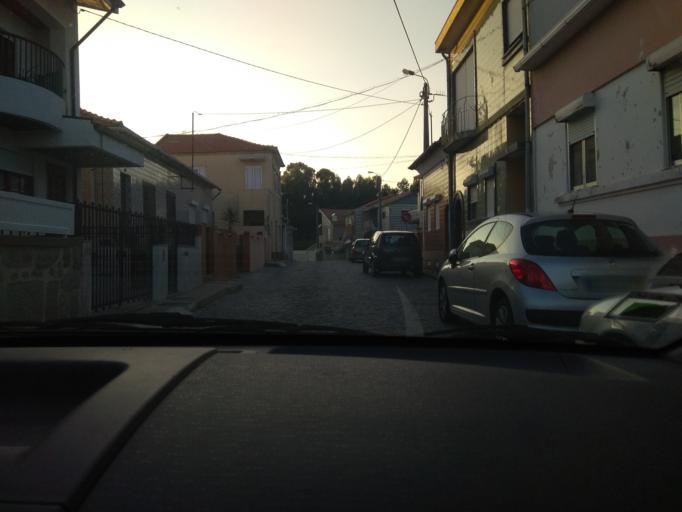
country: PT
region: Porto
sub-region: Matosinhos
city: Guifoes
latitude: 41.2008
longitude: -8.6604
